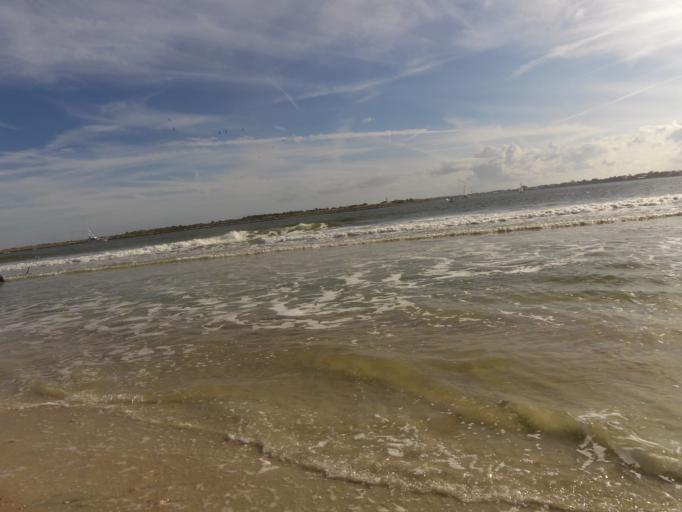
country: US
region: Florida
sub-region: Saint Johns County
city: Saint Augustine
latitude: 29.9105
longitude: -81.2947
